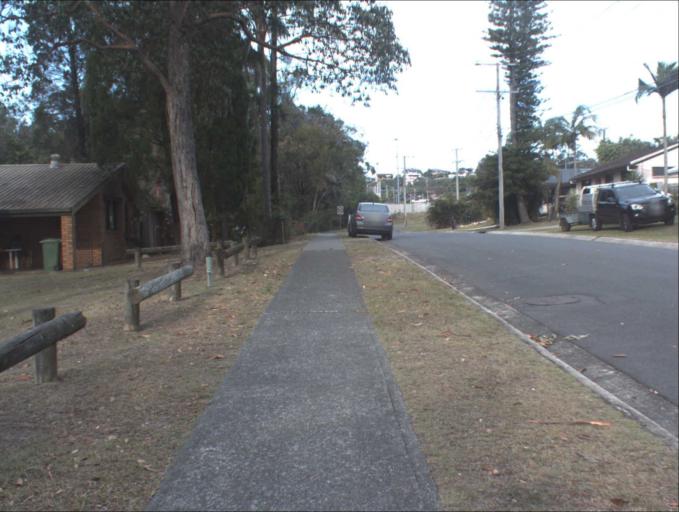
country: AU
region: Queensland
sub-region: Logan
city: Springwood
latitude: -27.6163
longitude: 153.1296
